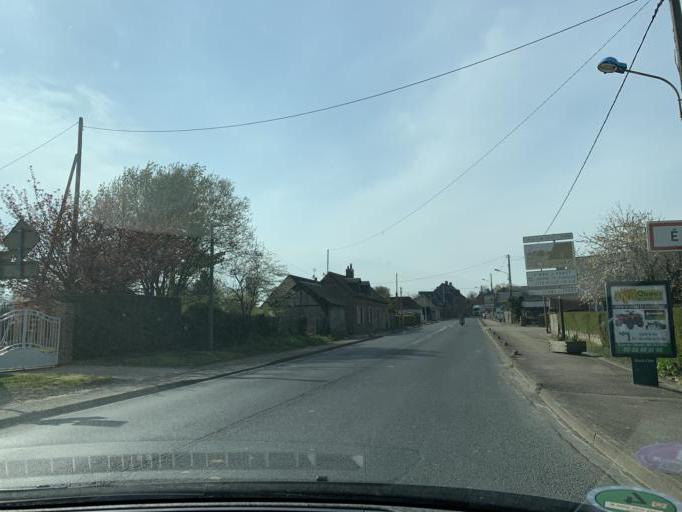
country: FR
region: Haute-Normandie
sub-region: Departement de l'Eure
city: Les Andelys
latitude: 49.3080
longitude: 1.4368
